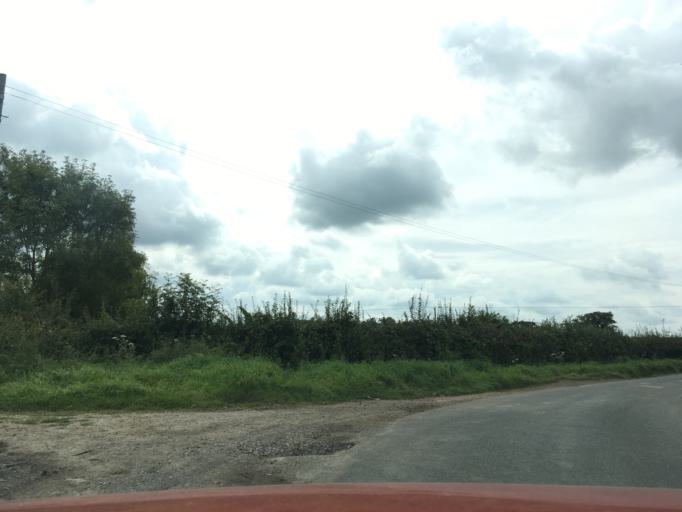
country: GB
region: England
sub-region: South Gloucestershire
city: Charfield
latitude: 51.6448
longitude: -2.4273
